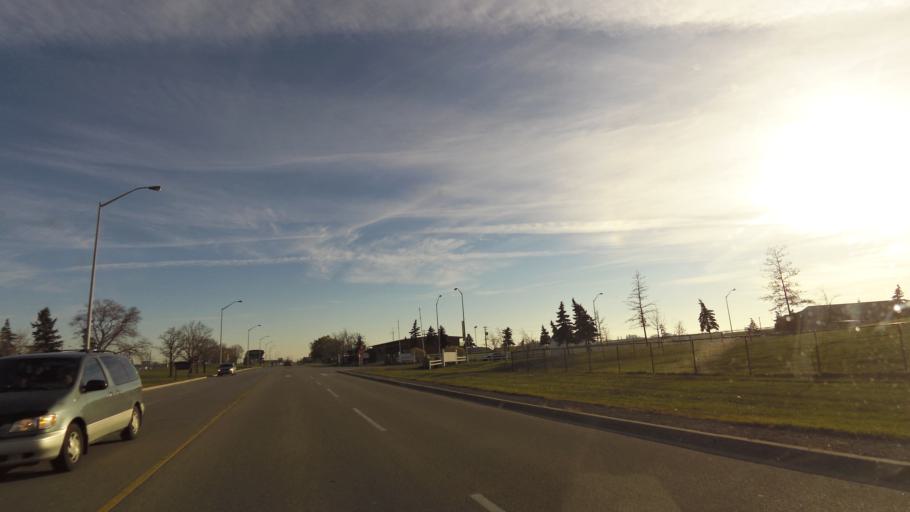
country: CA
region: Ontario
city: Etobicoke
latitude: 43.7119
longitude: -79.5944
